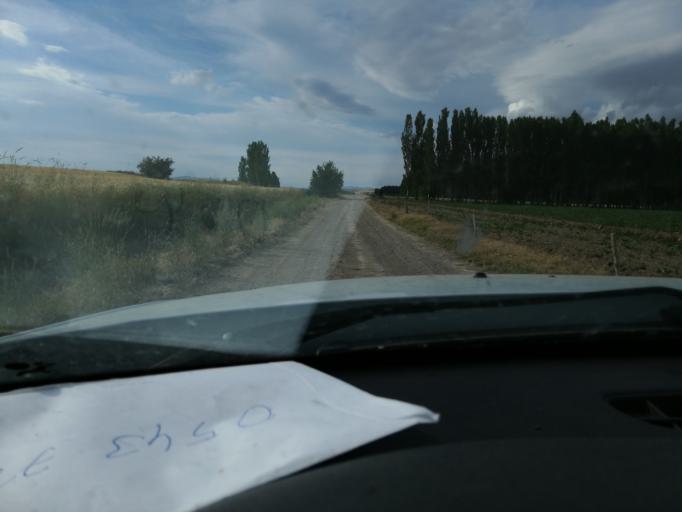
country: TR
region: Kirsehir
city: Kirsehir
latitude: 39.0020
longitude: 34.1240
